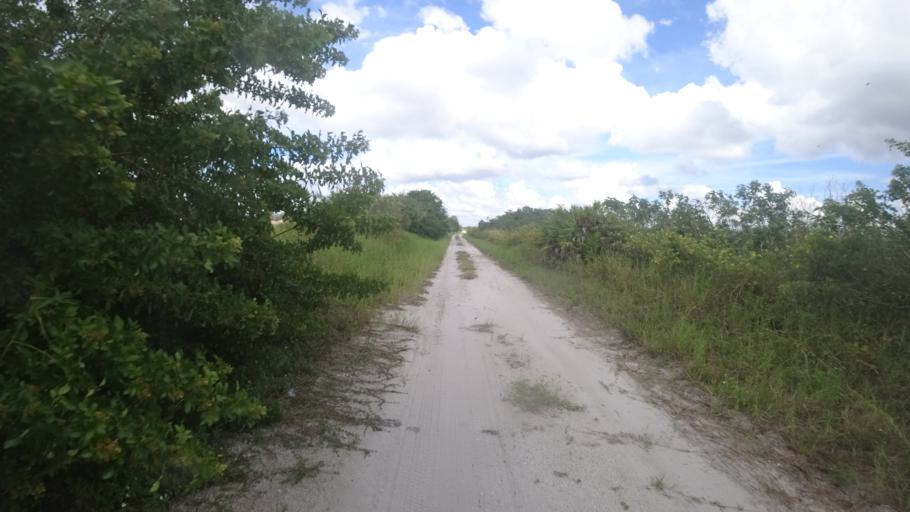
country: US
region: Florida
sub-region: Hillsborough County
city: Wimauma
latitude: 27.5813
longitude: -82.2673
